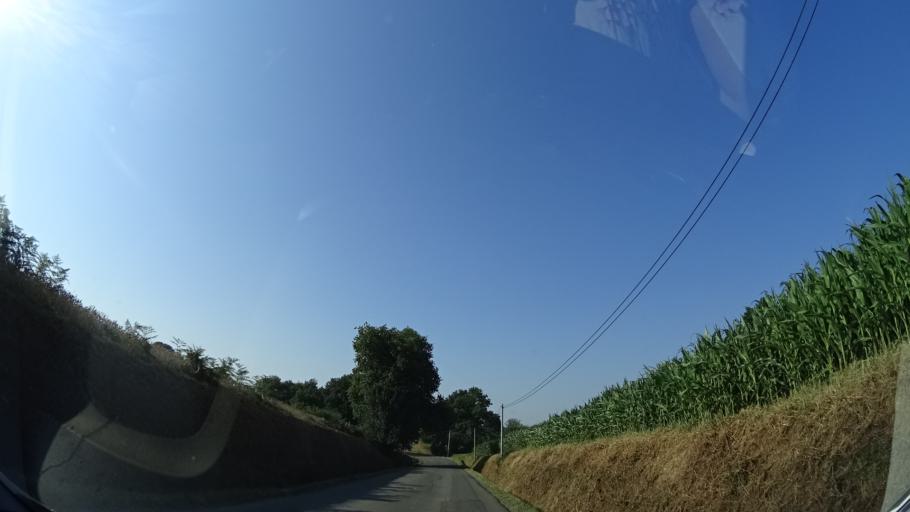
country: FR
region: Brittany
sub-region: Departement d'Ille-et-Vilaine
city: Pace
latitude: 48.1808
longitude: -1.7943
